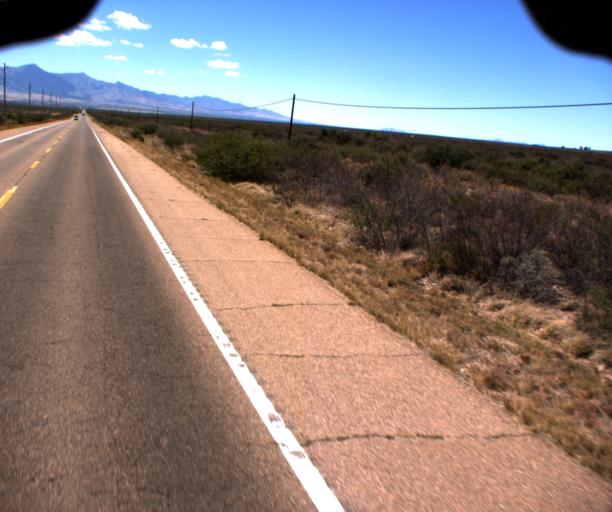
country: US
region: Arizona
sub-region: Cochise County
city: Naco
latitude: 31.3729
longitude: -109.9838
